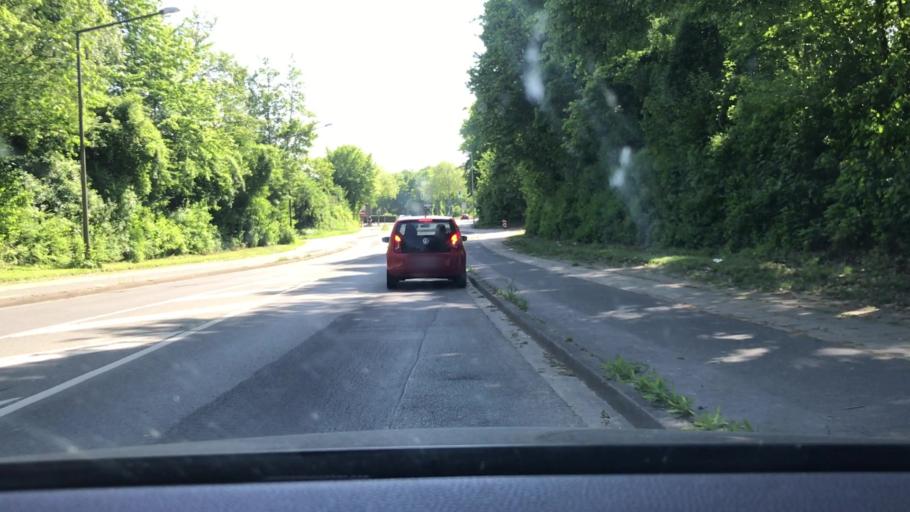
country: DE
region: North Rhine-Westphalia
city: Herten
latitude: 51.6107
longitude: 7.1447
